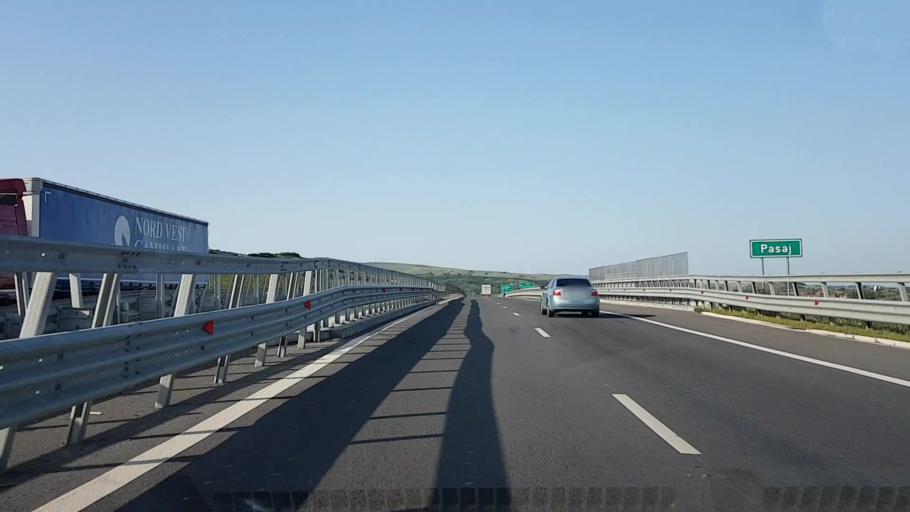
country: RO
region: Alba
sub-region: Comuna Miraslau
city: Miraslau
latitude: 46.3716
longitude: 23.7426
